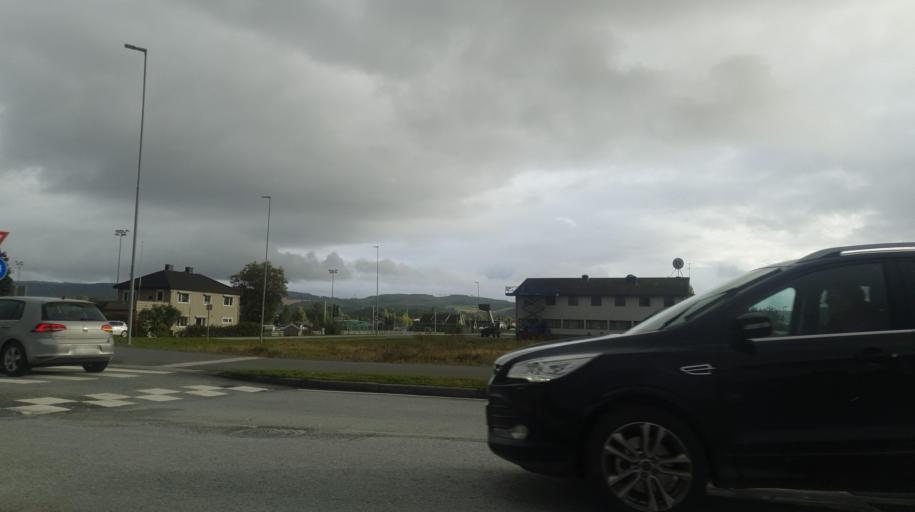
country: NO
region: Nord-Trondelag
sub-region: Verdal
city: Verdal
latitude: 63.7873
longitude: 11.4700
